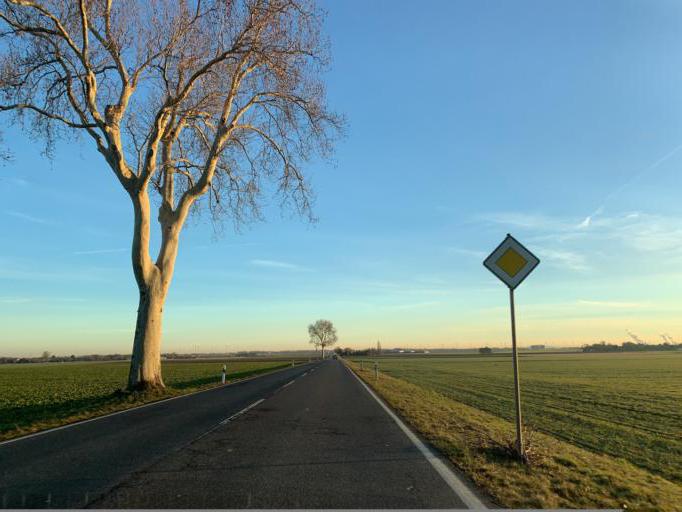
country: DE
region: North Rhine-Westphalia
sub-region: Regierungsbezirk Koln
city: Titz
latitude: 50.9722
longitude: 6.3901
